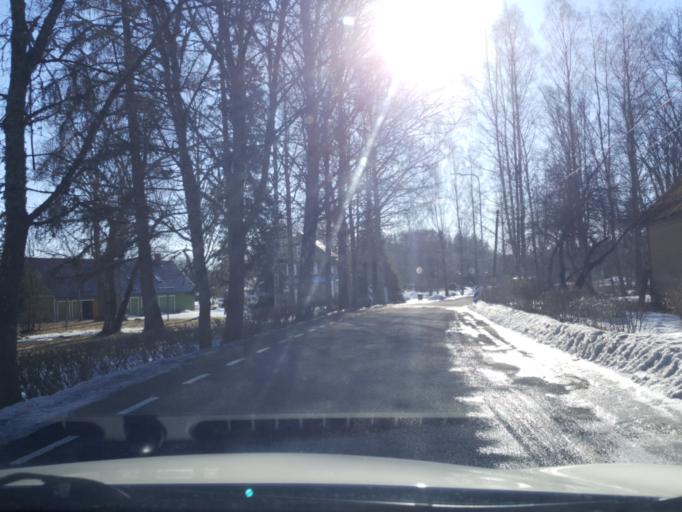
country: EE
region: Viljandimaa
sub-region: Vohma linn
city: Vohma
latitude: 58.5203
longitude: 25.6257
